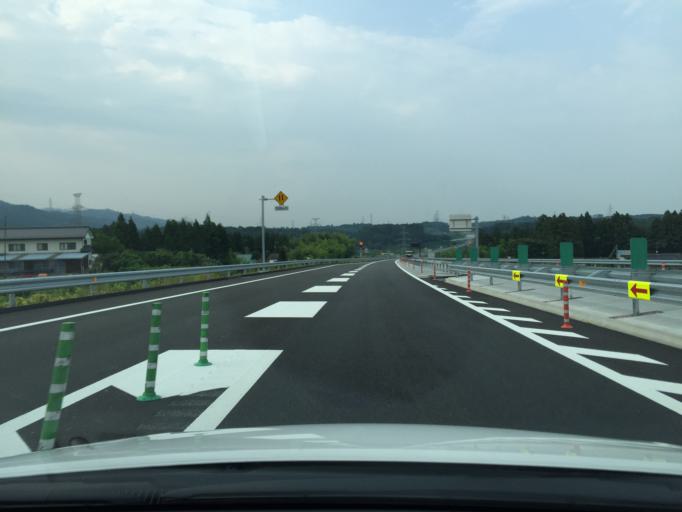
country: JP
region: Fukushima
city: Namie
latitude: 37.5013
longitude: 140.9424
